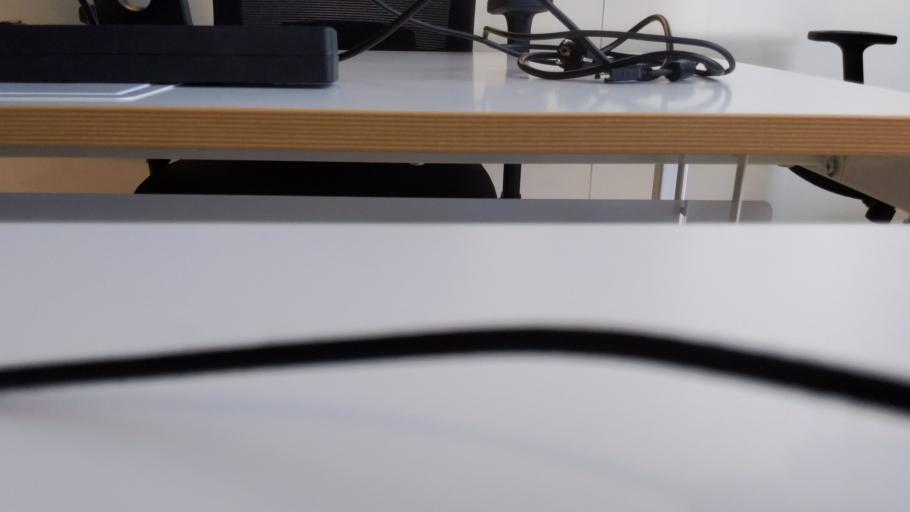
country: RU
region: Moskovskaya
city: Shevlyakovo
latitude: 56.4034
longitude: 36.8665
